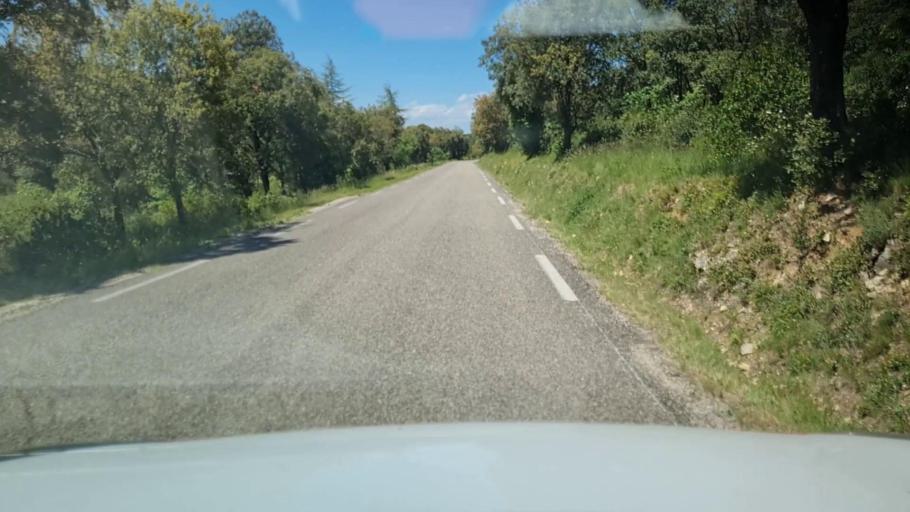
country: FR
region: Languedoc-Roussillon
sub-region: Departement du Gard
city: Clarensac
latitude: 43.8553
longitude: 4.2153
